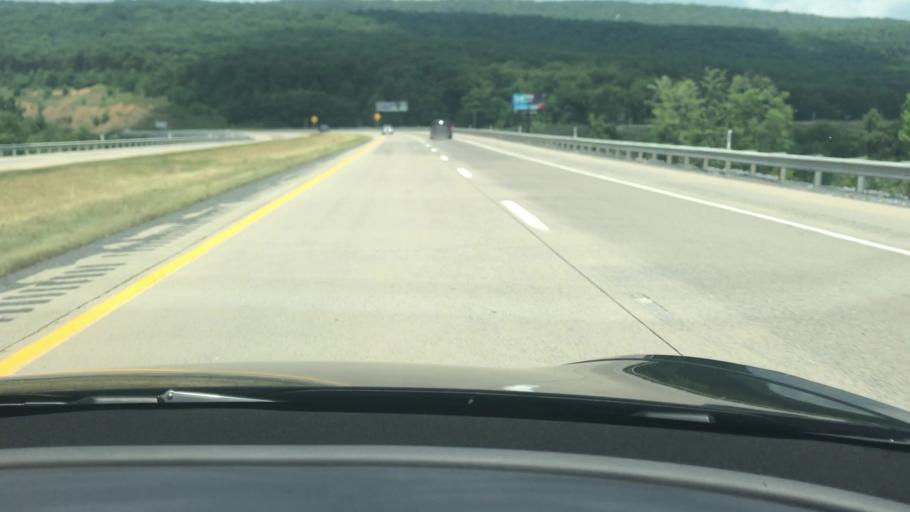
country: US
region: Pennsylvania
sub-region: Mifflin County
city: Milroy
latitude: 40.7266
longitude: -77.6041
